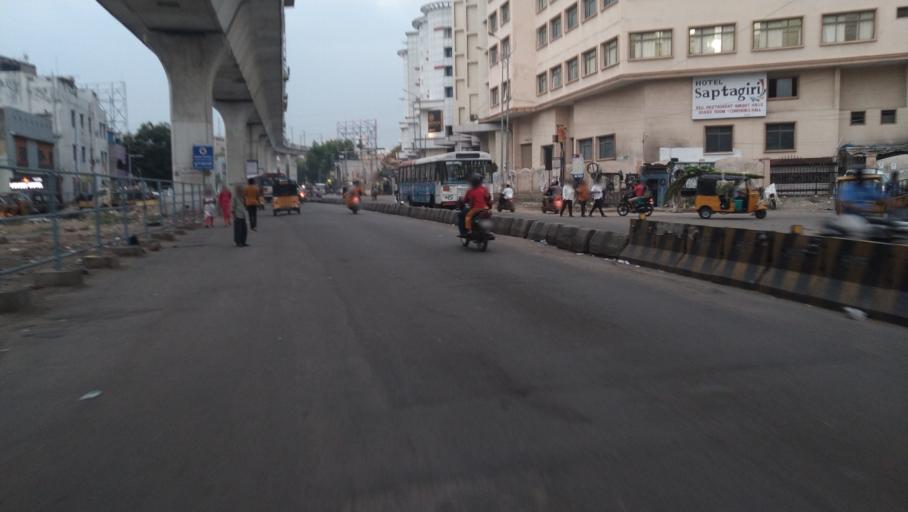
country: IN
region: Telangana
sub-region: Hyderabad
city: Malkajgiri
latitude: 17.4375
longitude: 78.4997
